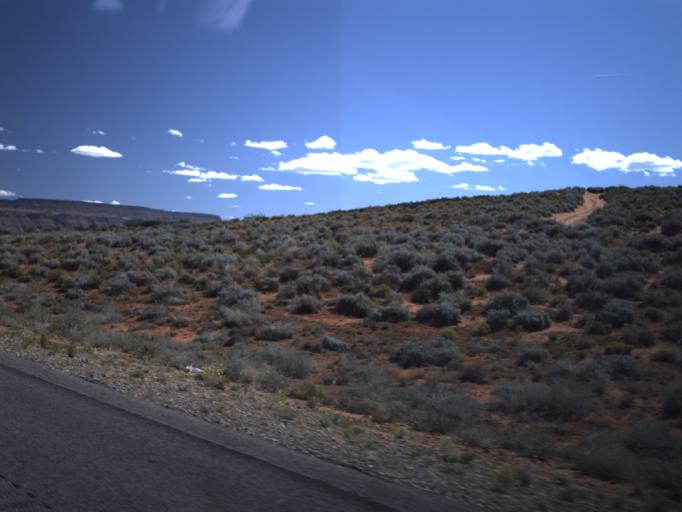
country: US
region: Utah
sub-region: Washington County
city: Washington
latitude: 37.1083
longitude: -113.4035
